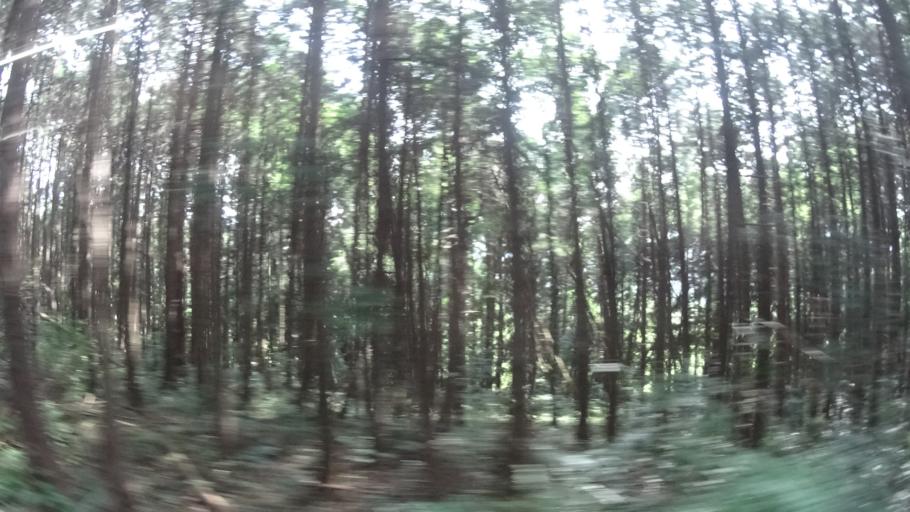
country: JP
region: Tochigi
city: Kanuma
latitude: 36.6243
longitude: 139.7322
